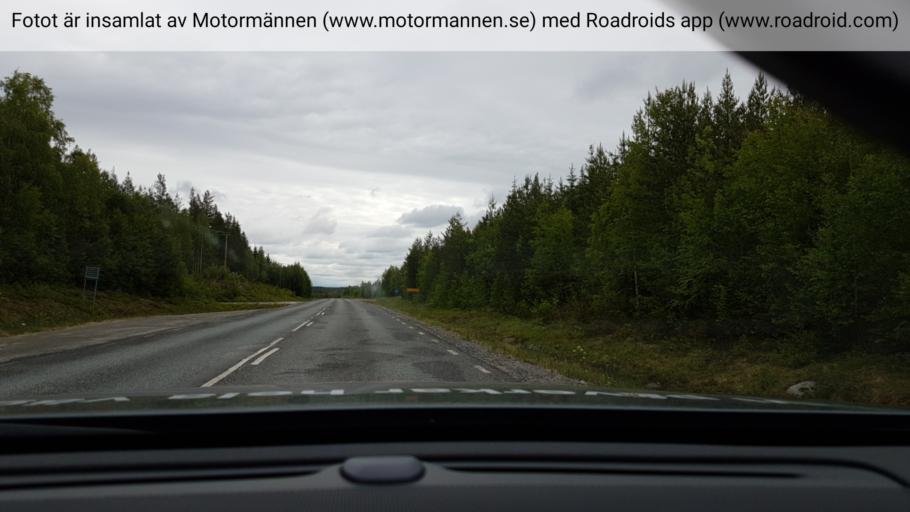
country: SE
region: Vaesterbotten
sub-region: Lycksele Kommun
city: Lycksele
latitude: 64.5310
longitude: 18.4637
